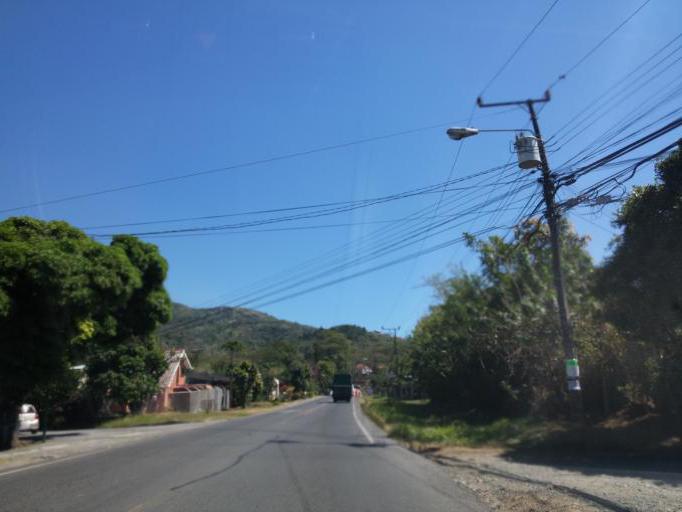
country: CR
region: Heredia
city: Colon
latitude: 9.9099
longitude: -84.2390
